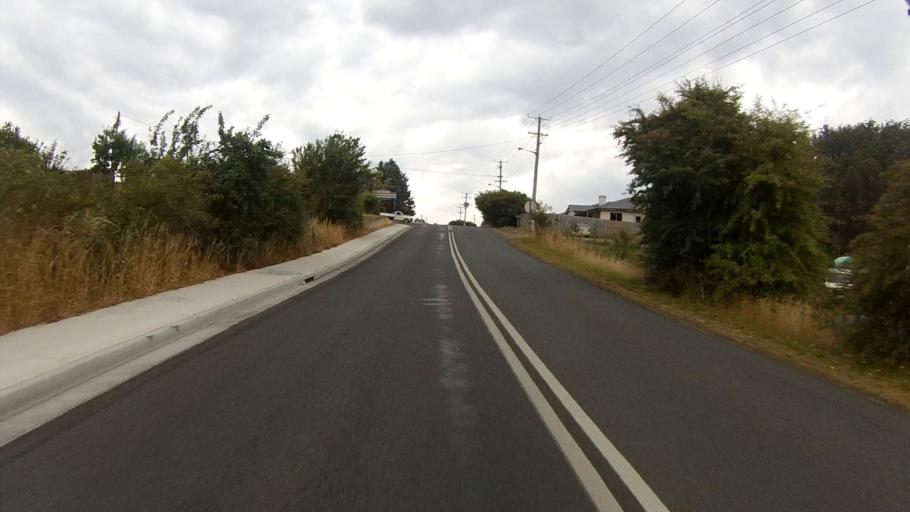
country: AU
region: Tasmania
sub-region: Huon Valley
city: Cygnet
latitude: -43.1538
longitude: 147.0727
